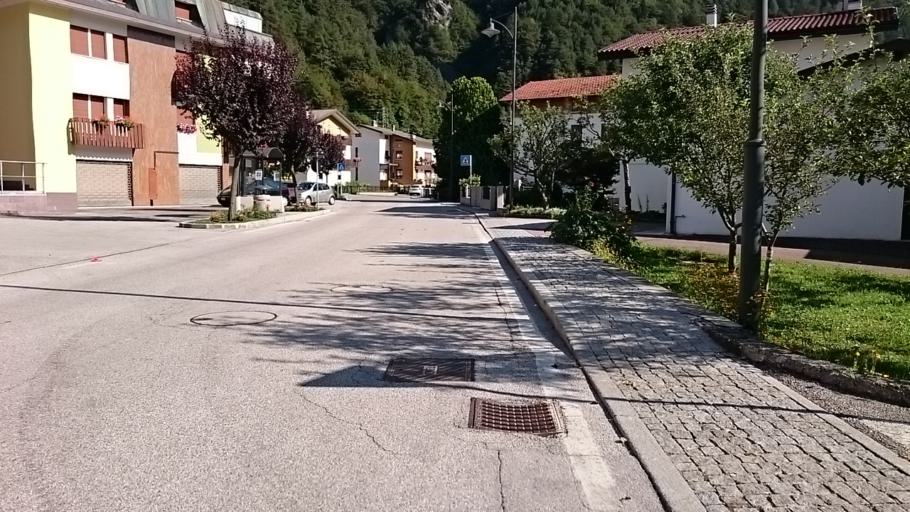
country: IT
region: Veneto
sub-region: Provincia di Belluno
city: Soverzene
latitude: 46.2037
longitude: 12.3031
